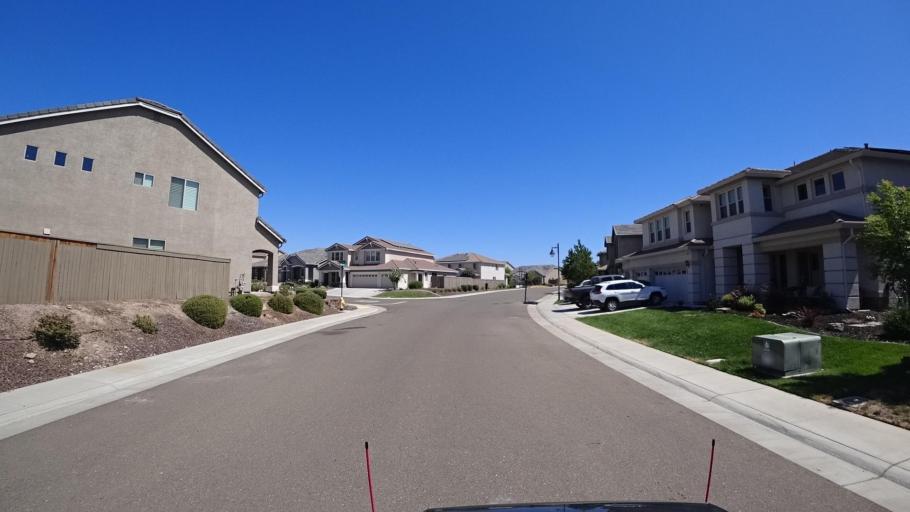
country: US
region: California
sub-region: Placer County
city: Rocklin
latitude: 38.8240
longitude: -121.2858
